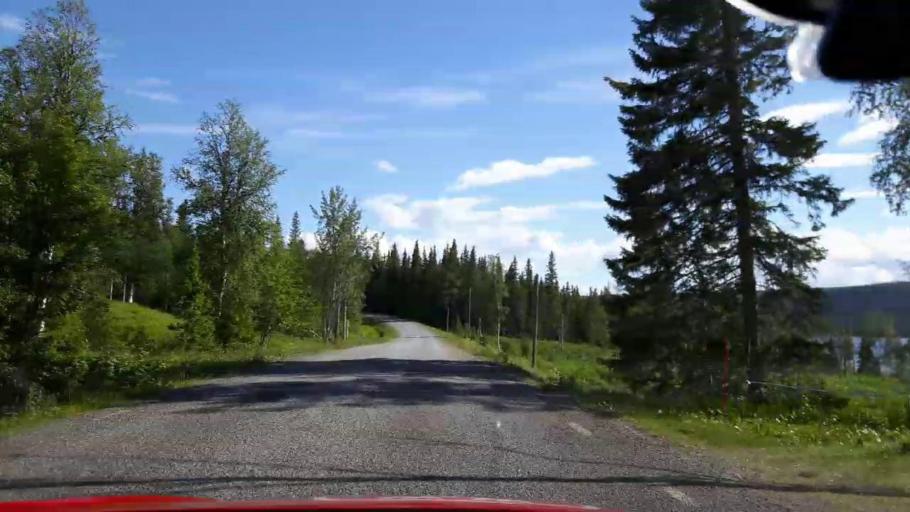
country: SE
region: Jaemtland
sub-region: Krokoms Kommun
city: Valla
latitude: 63.7245
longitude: 14.1225
